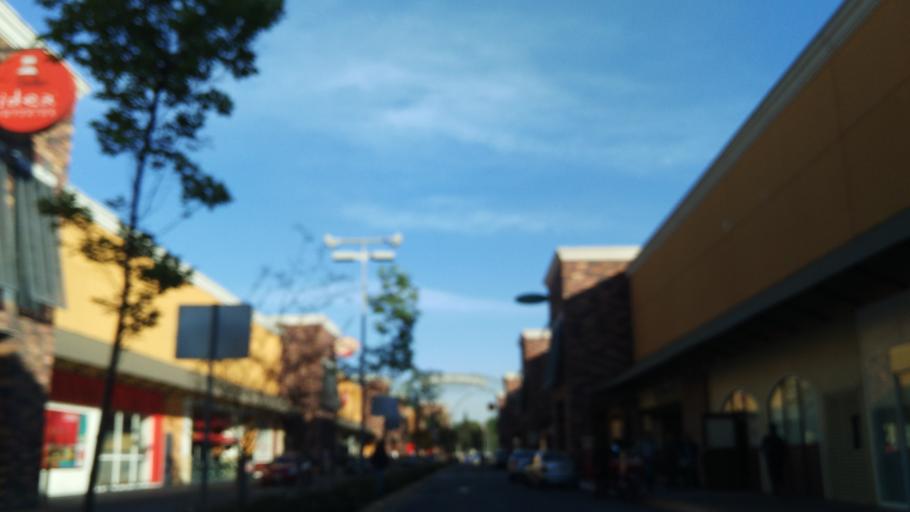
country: MX
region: Mexico City
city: Xochimilco
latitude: 19.2955
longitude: -99.1095
